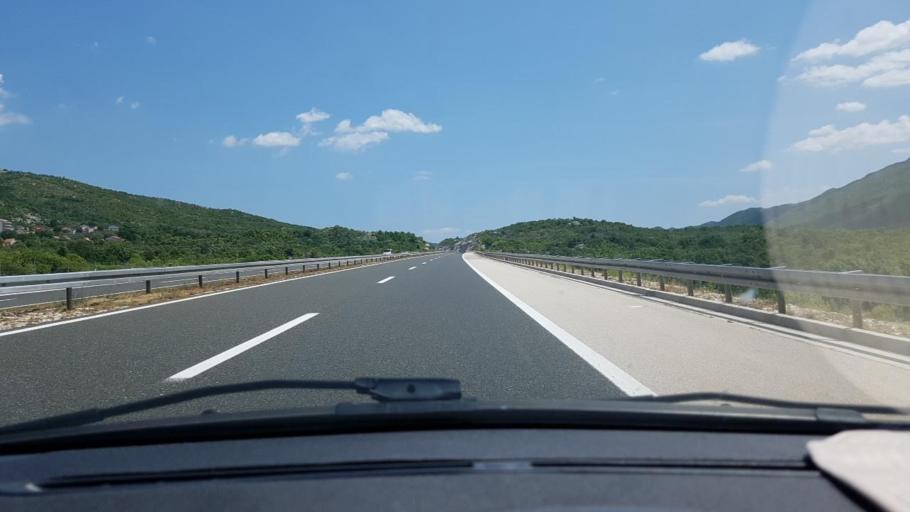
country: HR
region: Splitsko-Dalmatinska
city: Grubine
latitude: 43.3849
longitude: 17.0680
